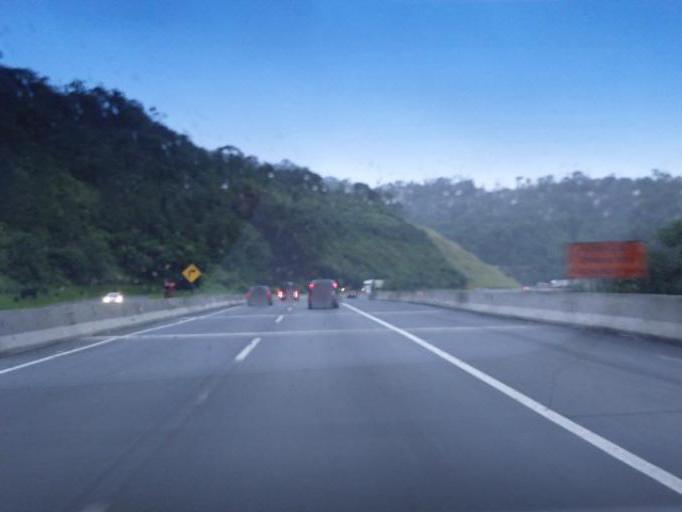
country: BR
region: Sao Paulo
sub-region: Miracatu
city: Miracatu
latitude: -24.1237
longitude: -47.2712
